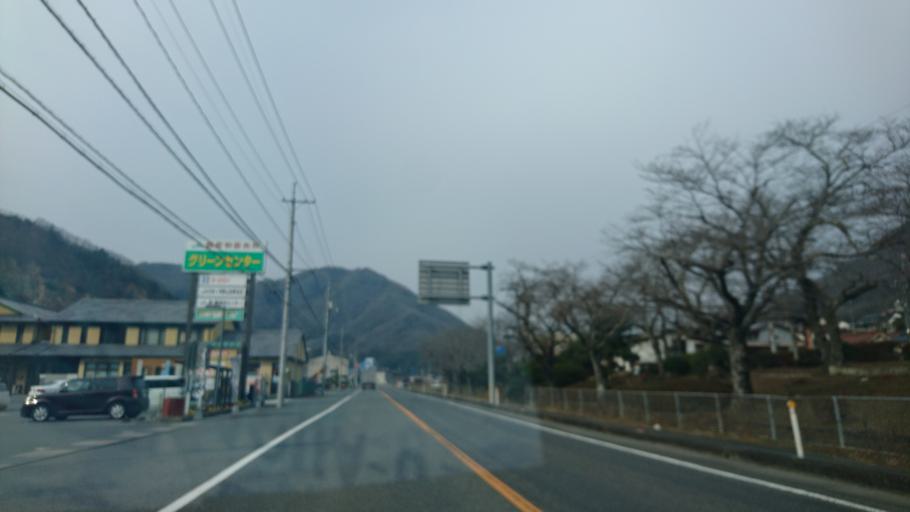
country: JP
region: Okayama
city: Takahashi
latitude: 34.8252
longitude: 133.6153
